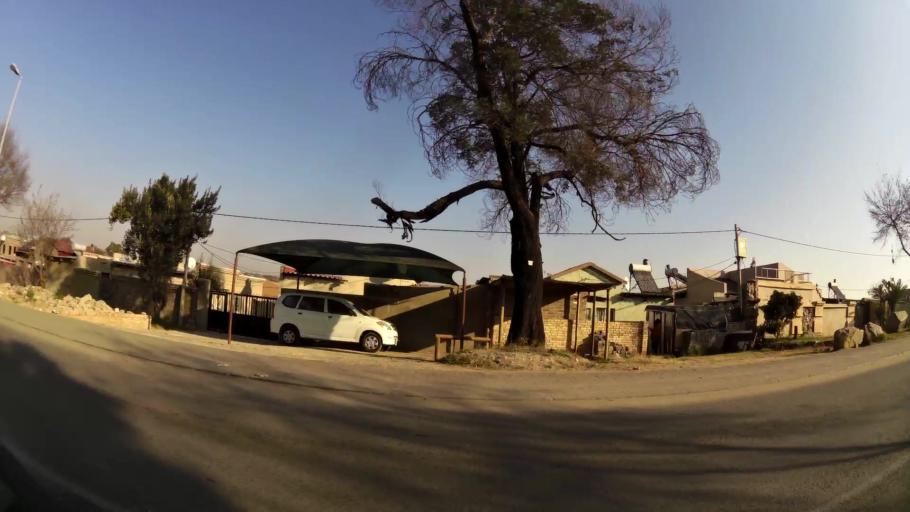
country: ZA
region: Gauteng
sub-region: City of Johannesburg Metropolitan Municipality
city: Modderfontein
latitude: -26.0935
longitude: 28.1120
